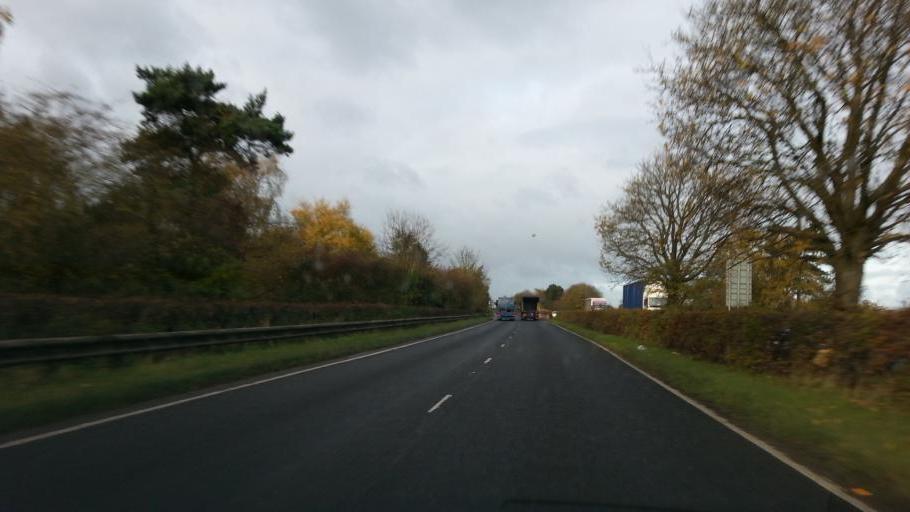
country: GB
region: England
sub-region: Leicestershire
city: Kirby Muxloe
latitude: 52.6641
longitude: -1.2256
